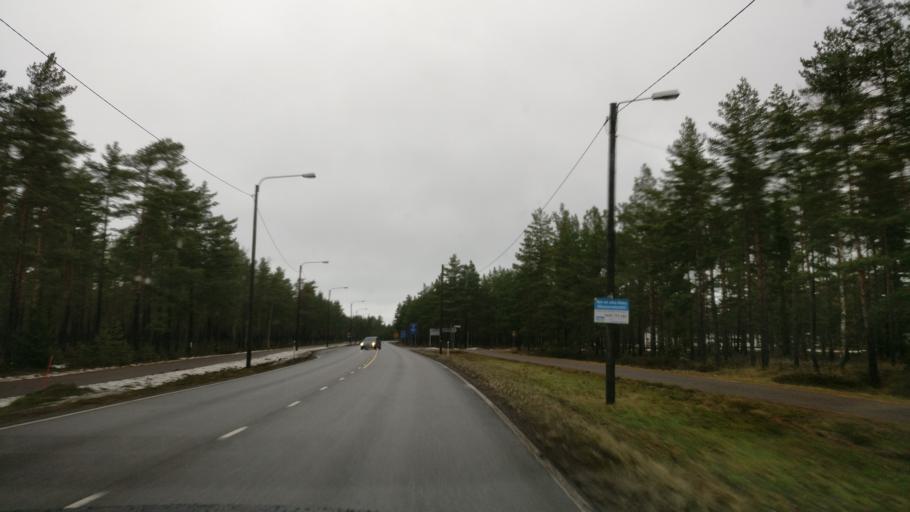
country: FI
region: Uusimaa
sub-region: Raaseporin
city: Hanko
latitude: 59.8454
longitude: 23.0072
